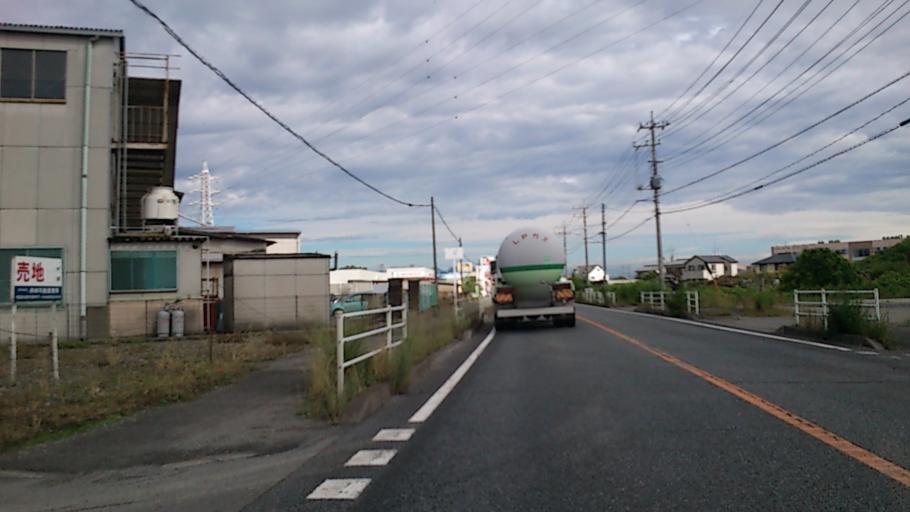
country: JP
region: Saitama
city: Honjo
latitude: 36.2375
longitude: 139.2062
